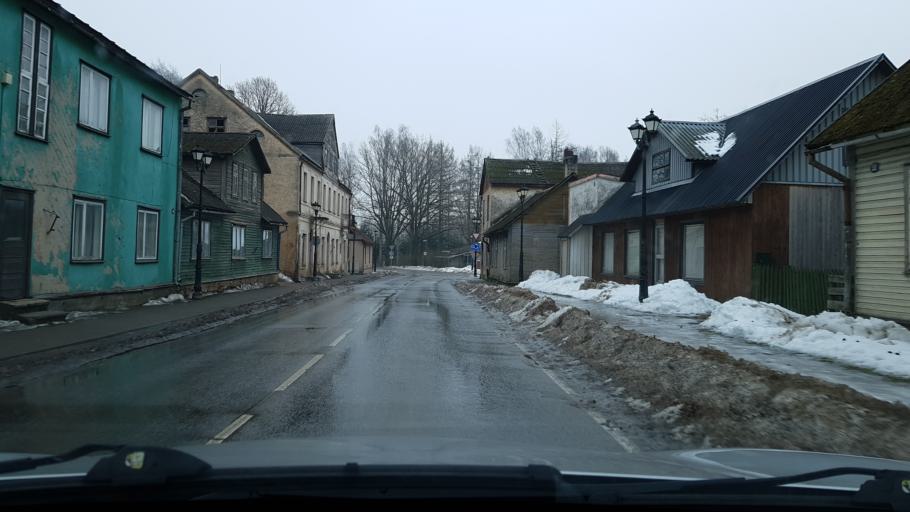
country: EE
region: Valgamaa
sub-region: Torva linn
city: Torva
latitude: 58.2354
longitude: 25.8620
